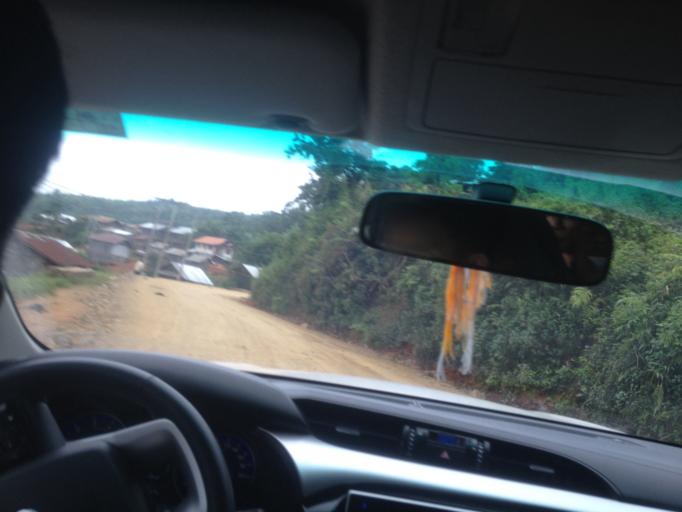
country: TH
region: Nan
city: Chaloem Phra Kiat
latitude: 19.9826
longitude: 101.1439
